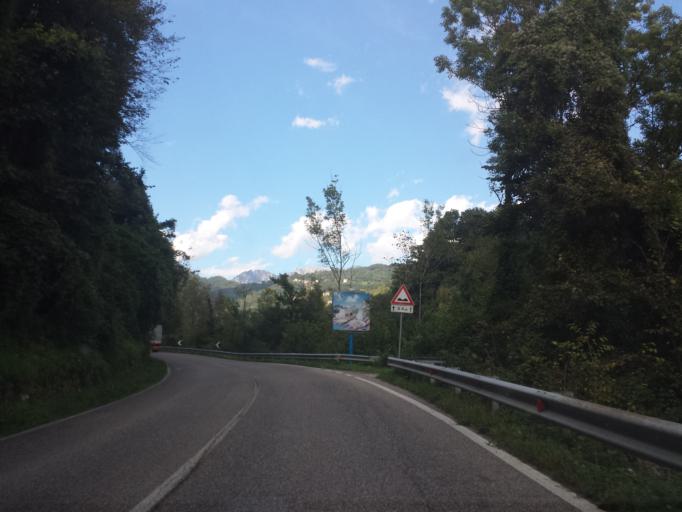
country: IT
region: Veneto
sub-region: Provincia di Vicenza
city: San Quirico
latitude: 45.6919
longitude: 11.2593
